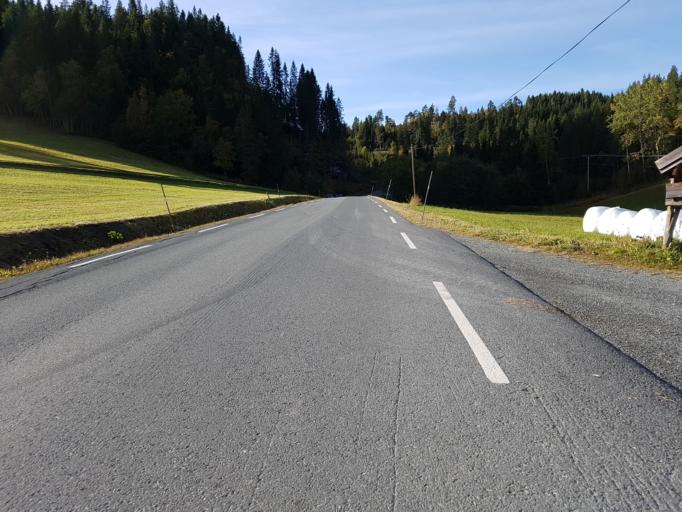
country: NO
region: Sor-Trondelag
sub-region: Klaebu
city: Klaebu
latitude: 63.3453
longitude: 10.5415
